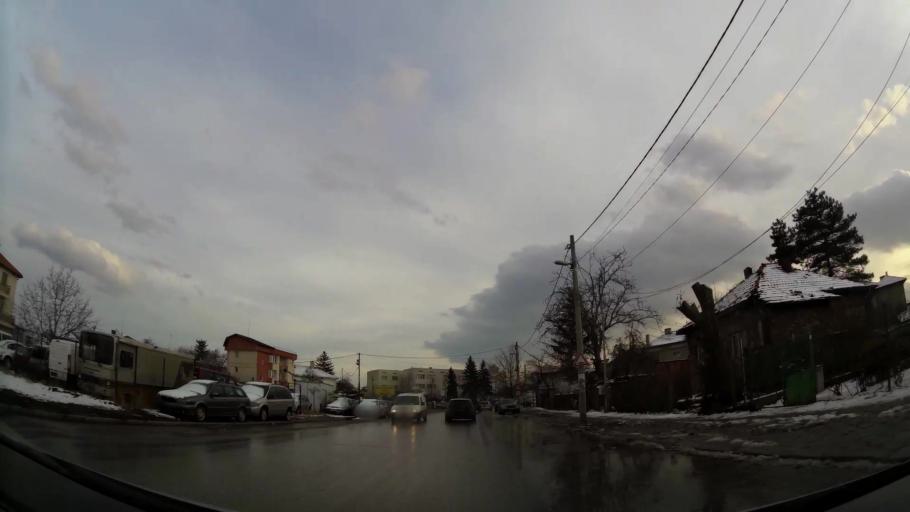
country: BG
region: Sofia-Capital
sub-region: Stolichna Obshtina
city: Sofia
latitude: 42.7220
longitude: 23.3433
